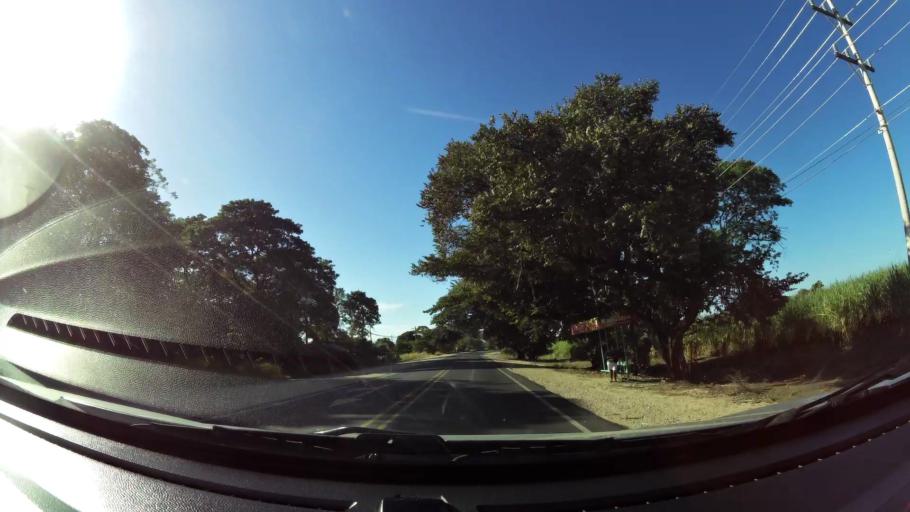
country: CR
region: Guanacaste
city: Belen
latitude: 10.4414
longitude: -85.5565
